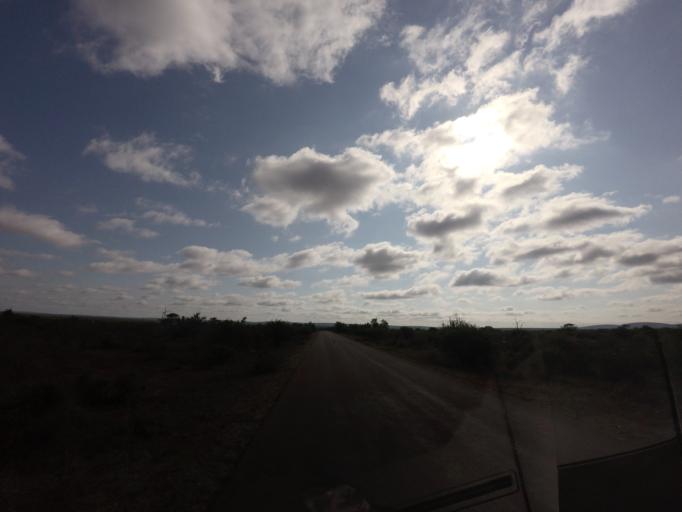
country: ZA
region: Mpumalanga
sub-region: Ehlanzeni District
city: Komatipoort
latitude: -25.1658
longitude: 31.9257
